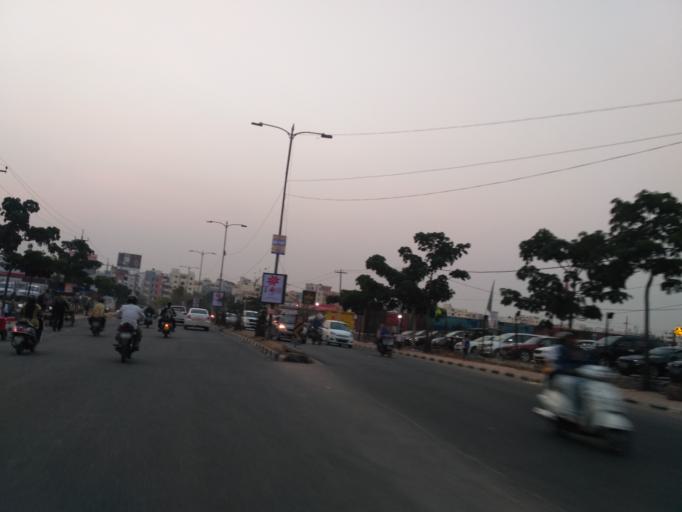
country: IN
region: Telangana
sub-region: Rangareddi
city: Kukatpalli
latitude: 17.4424
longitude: 78.3958
